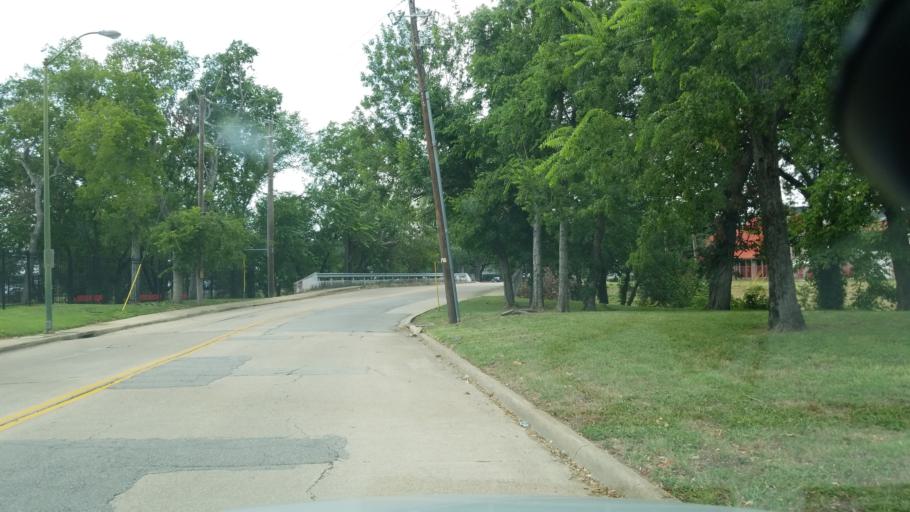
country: US
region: Texas
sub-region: Dallas County
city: Dallas
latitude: 32.8181
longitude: -96.8642
